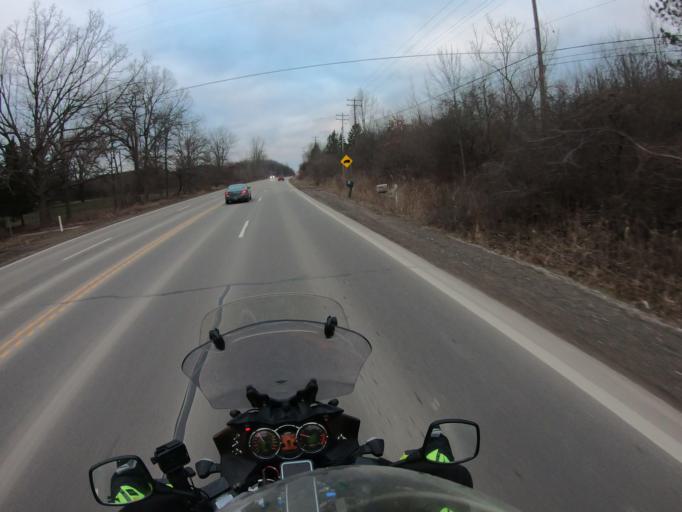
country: US
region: Michigan
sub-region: Oakland County
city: Holly
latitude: 42.8537
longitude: -83.5736
